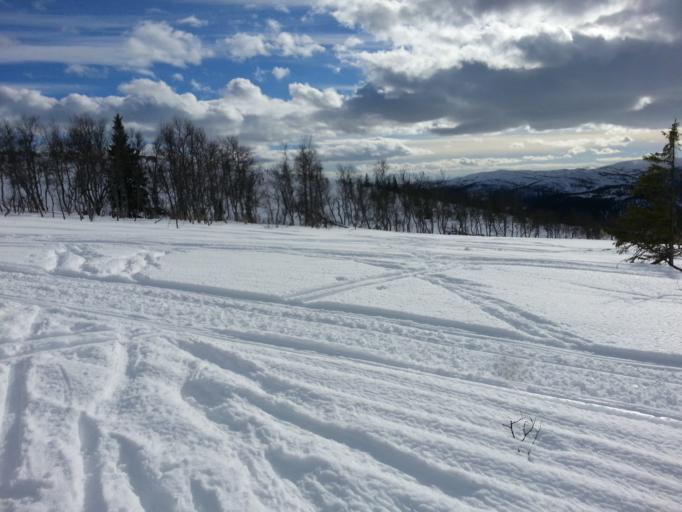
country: NO
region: Nord-Trondelag
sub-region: Royrvik
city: Royrvik
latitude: 64.8517
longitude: 14.1176
